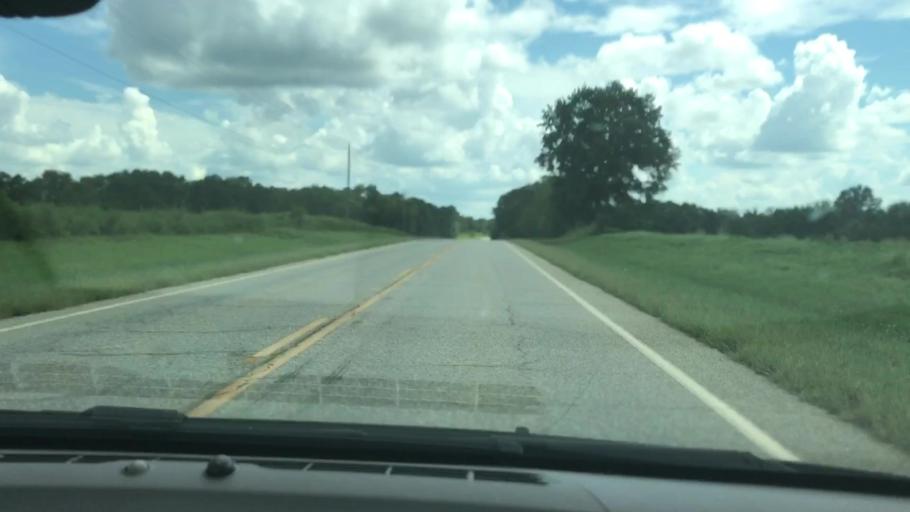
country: US
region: Georgia
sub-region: Clay County
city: Fort Gaines
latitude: 31.7185
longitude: -85.0431
